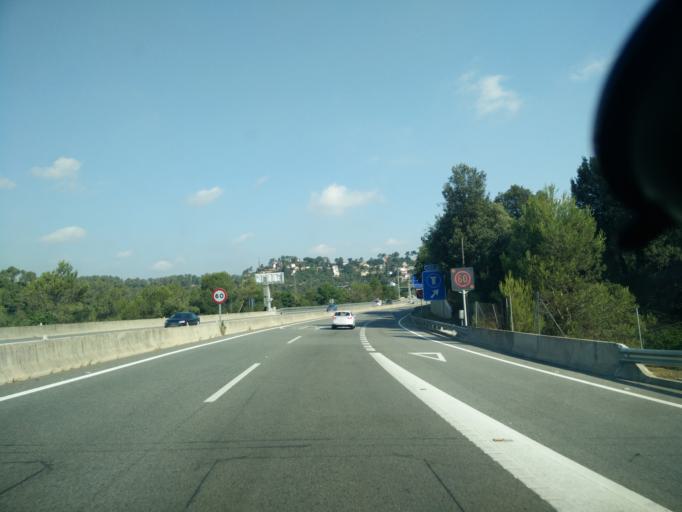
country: ES
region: Catalonia
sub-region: Provincia de Barcelona
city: Sant Cugat del Valles
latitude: 41.4342
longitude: 2.0766
